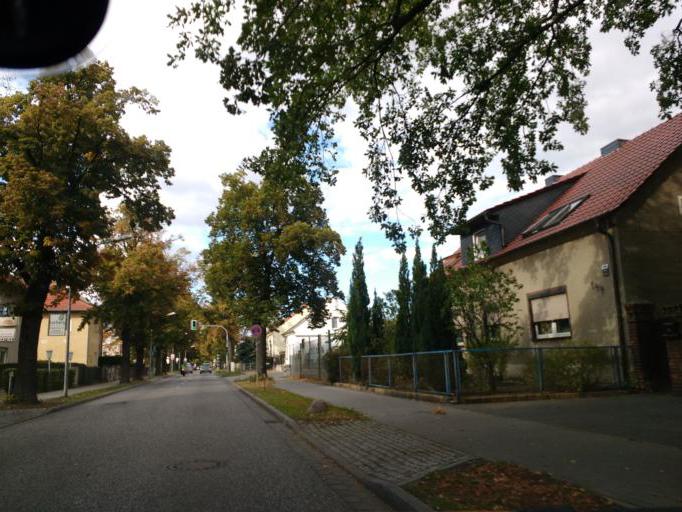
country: DE
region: Berlin
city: Lichtenrade
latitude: 52.3959
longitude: 13.4424
